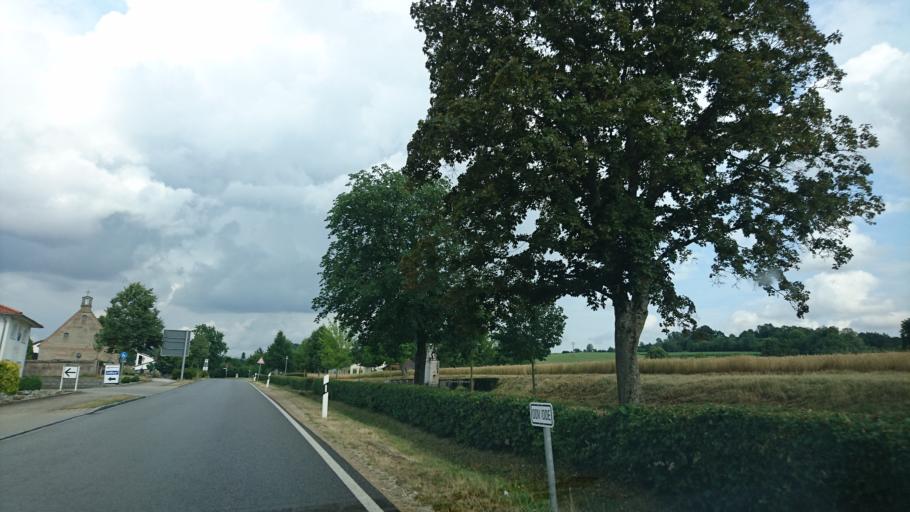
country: DE
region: Bavaria
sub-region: Regierungsbezirk Mittelfranken
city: Heideck
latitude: 49.1323
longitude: 11.1307
